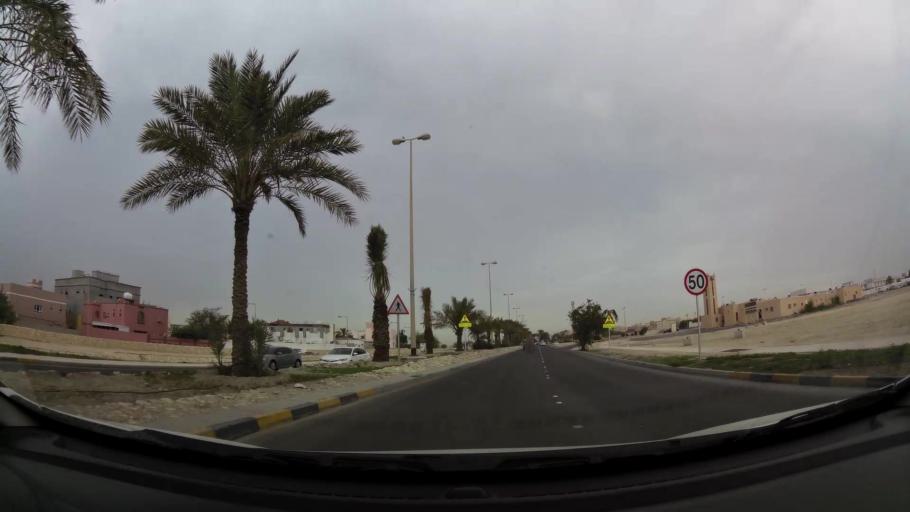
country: BH
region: Central Governorate
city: Dar Kulayb
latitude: 26.0691
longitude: 50.5078
